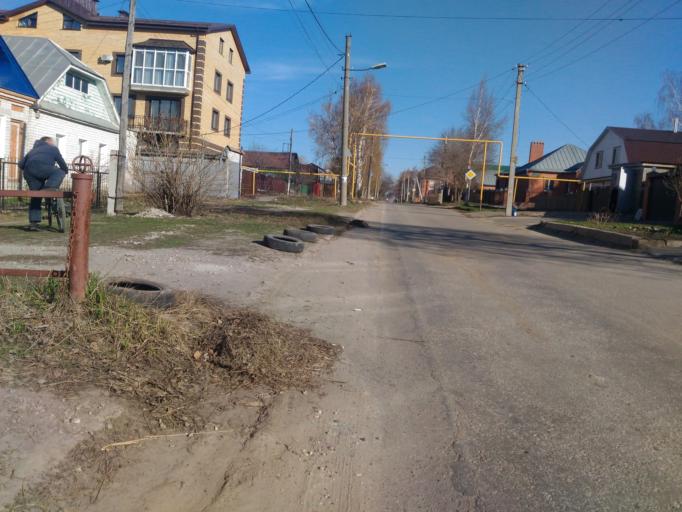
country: RU
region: Ulyanovsk
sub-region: Ulyanovskiy Rayon
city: Ulyanovsk
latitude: 54.3437
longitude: 48.3838
